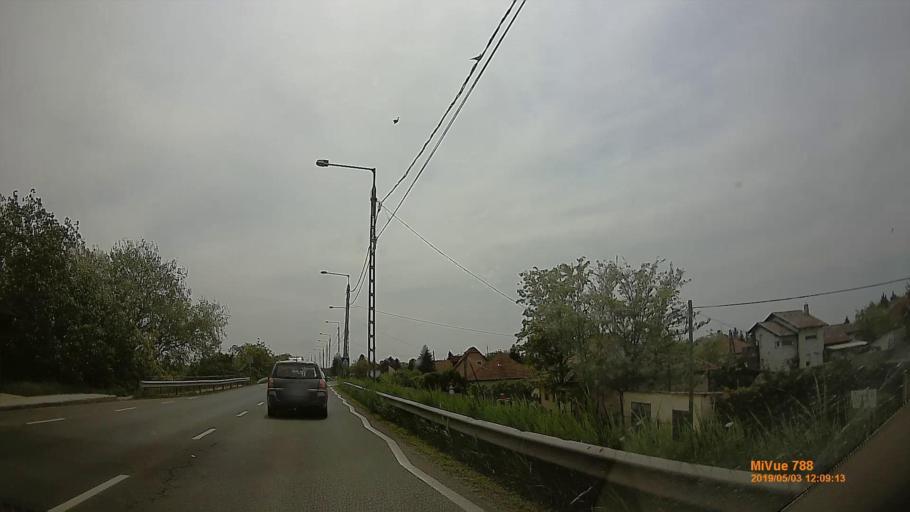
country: HU
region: Jasz-Nagykun-Szolnok
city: Szolnok
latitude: 47.1427
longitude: 20.2050
